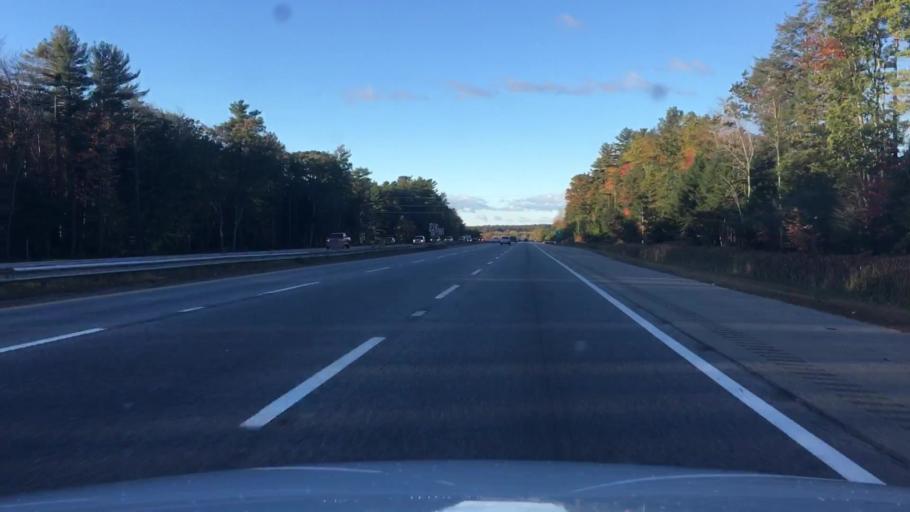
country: US
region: Maine
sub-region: York County
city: Biddeford
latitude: 43.5120
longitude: -70.4737
